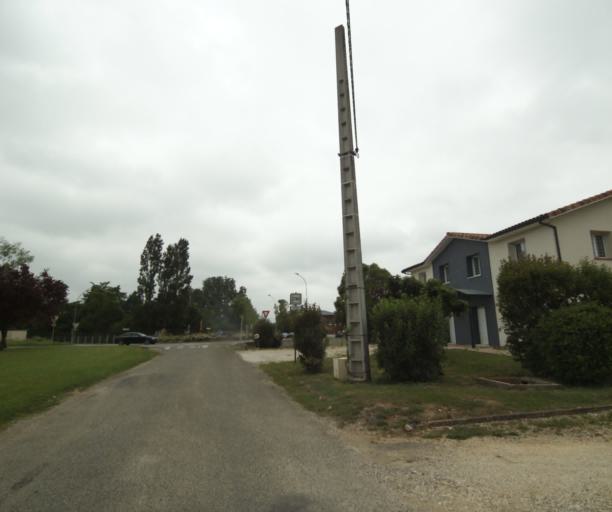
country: FR
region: Midi-Pyrenees
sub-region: Departement du Tarn-et-Garonne
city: Montauban
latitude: 43.9959
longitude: 1.3349
